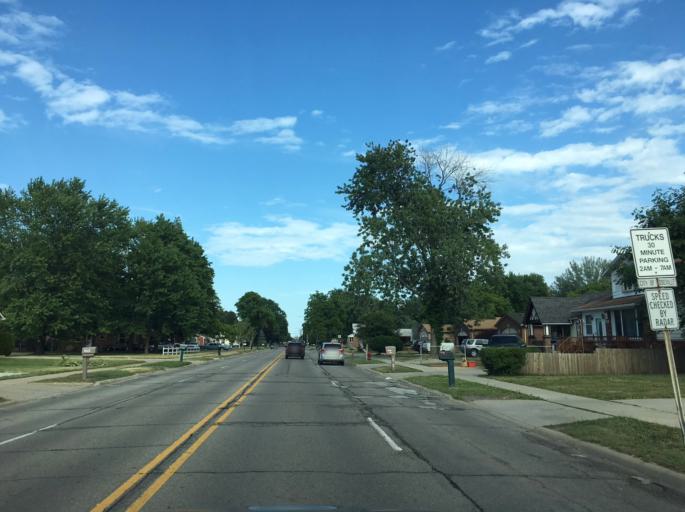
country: US
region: Michigan
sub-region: Macomb County
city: Fraser
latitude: 42.5319
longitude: -82.9280
